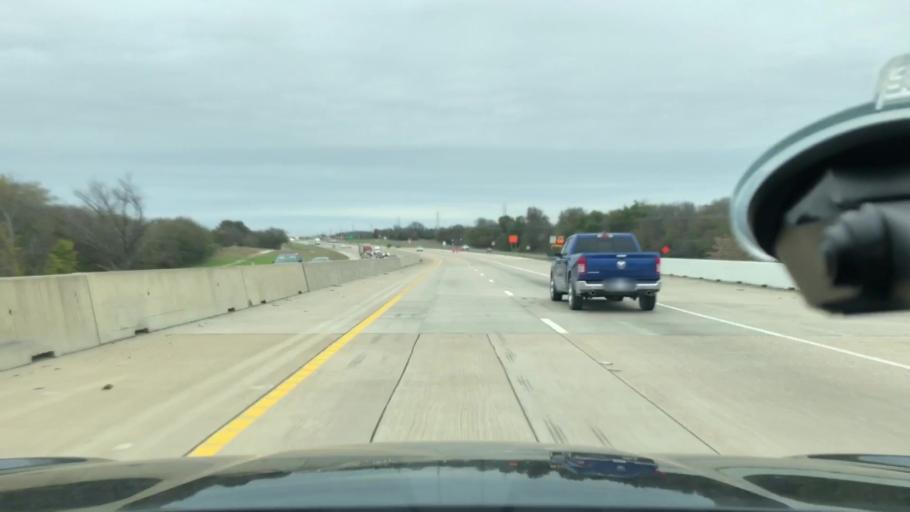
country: US
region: Texas
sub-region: Ellis County
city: Waxahachie
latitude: 32.3454
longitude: -96.8550
